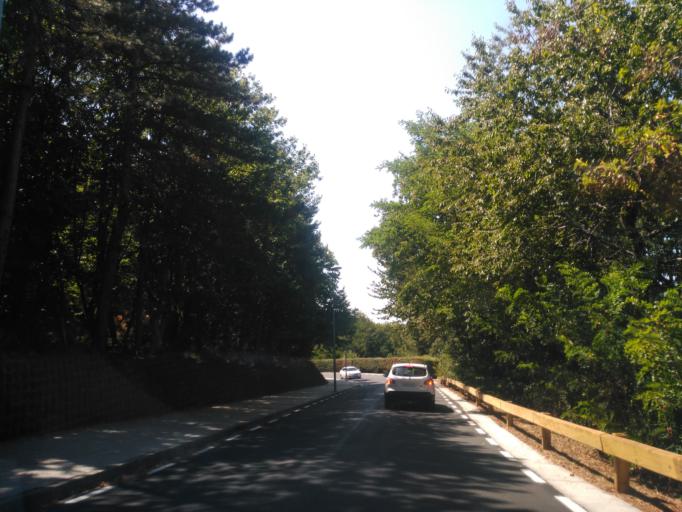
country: ES
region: Castille and Leon
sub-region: Provincia de Salamanca
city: Bejar
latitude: 40.3806
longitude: -5.7709
